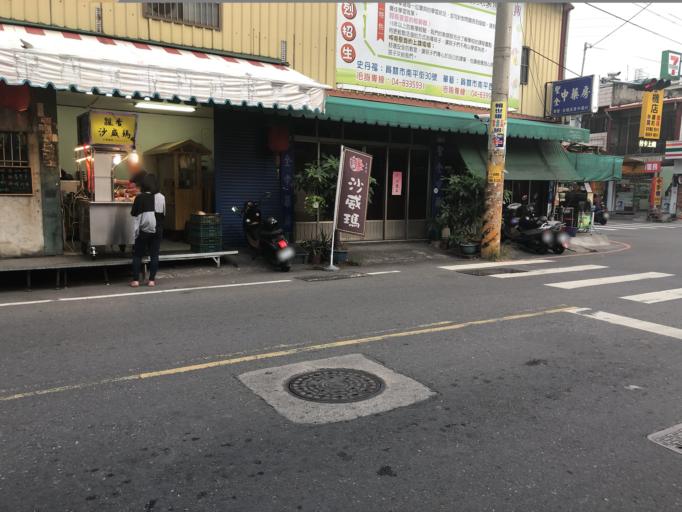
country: TW
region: Taiwan
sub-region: Nantou
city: Nantou
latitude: 23.9625
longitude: 120.5647
